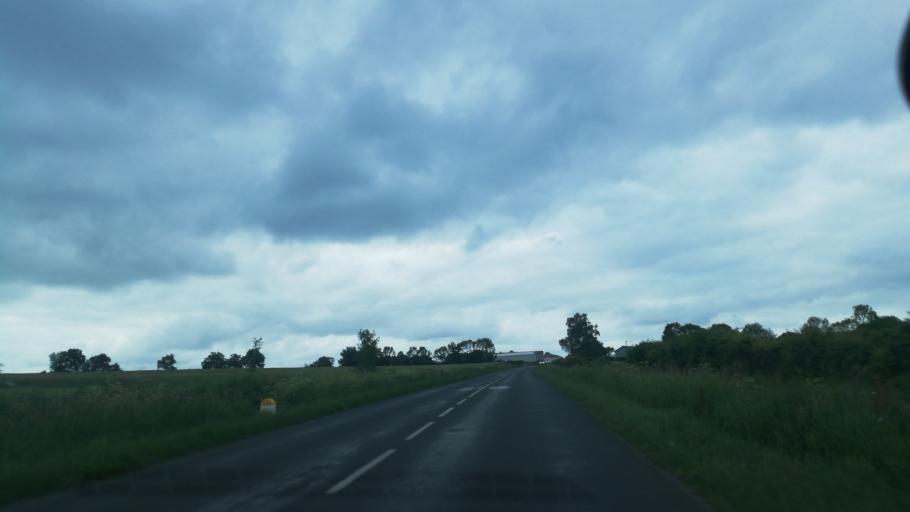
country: FR
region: Poitou-Charentes
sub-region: Departement des Deux-Sevres
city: Courlay
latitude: 46.7566
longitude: -0.5435
